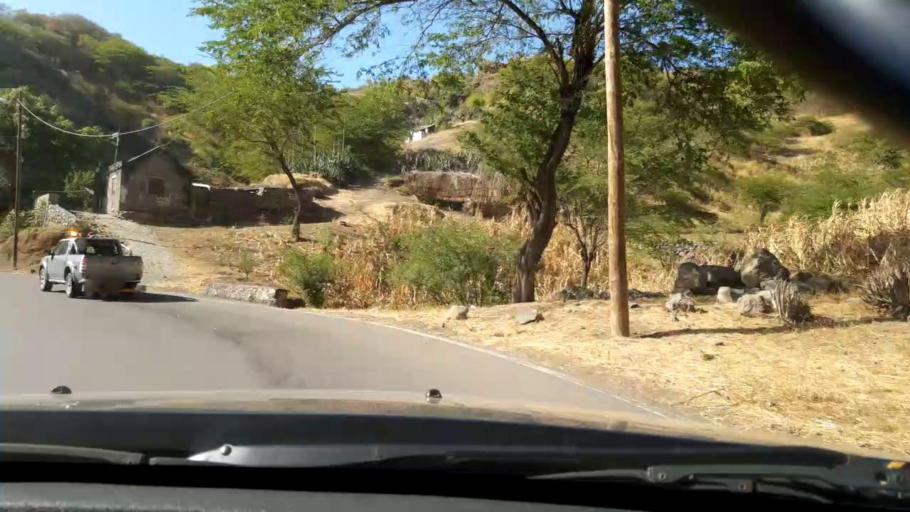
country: CV
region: Sao Lourenco dos Orgaos
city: Joao Teves
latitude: 15.0730
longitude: -23.5665
